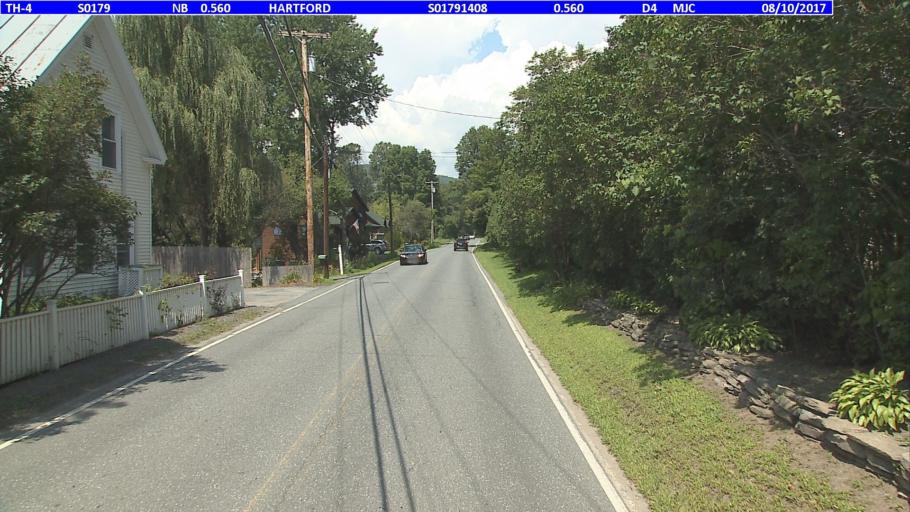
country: US
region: Vermont
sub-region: Windsor County
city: Woodstock
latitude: 43.6518
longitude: -72.4265
